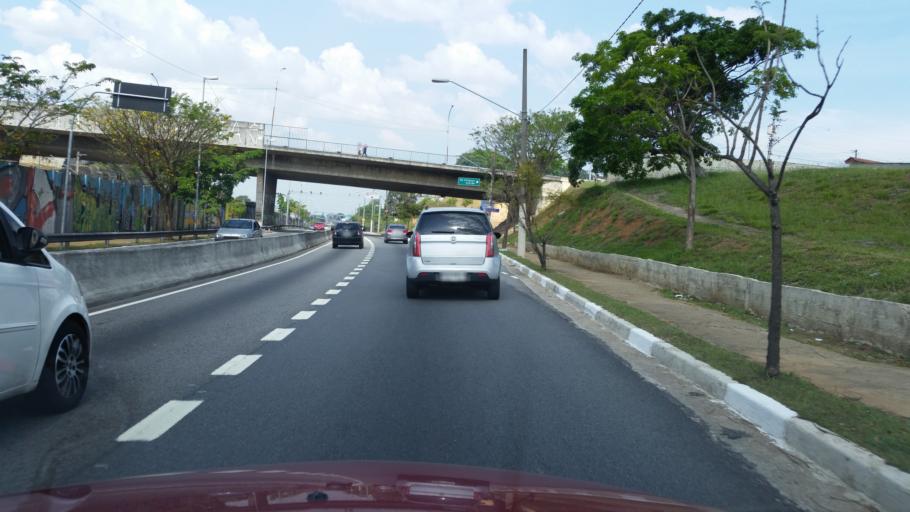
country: BR
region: Sao Paulo
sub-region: Guarulhos
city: Guarulhos
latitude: -23.5355
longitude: -46.4951
